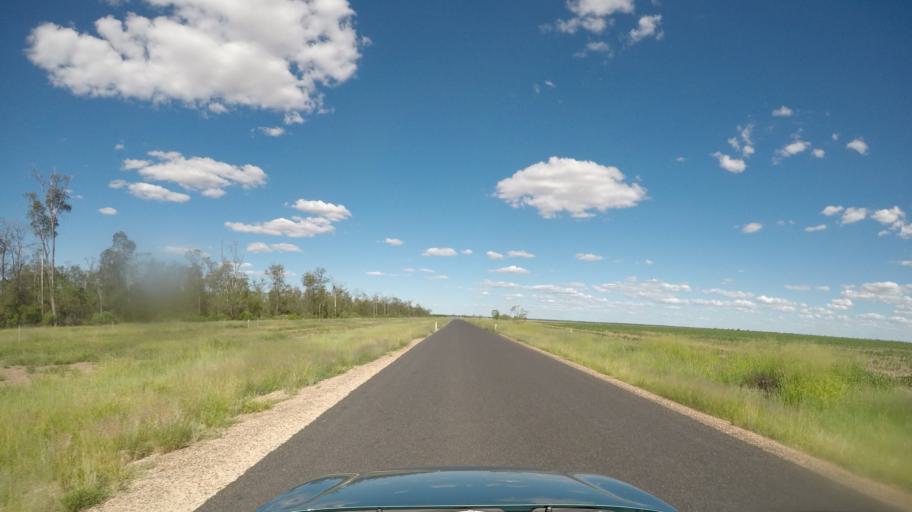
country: AU
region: Queensland
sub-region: Goondiwindi
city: Goondiwindi
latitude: -28.1733
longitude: 150.2372
